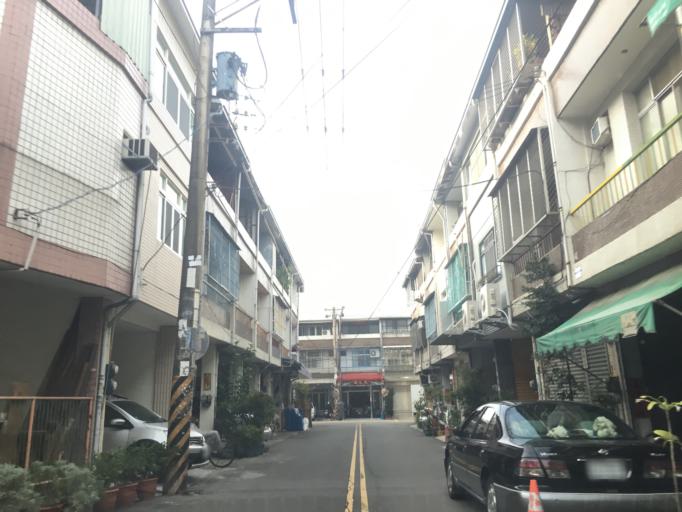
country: TW
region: Taiwan
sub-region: Taichung City
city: Taichung
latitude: 24.1928
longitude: 120.6960
